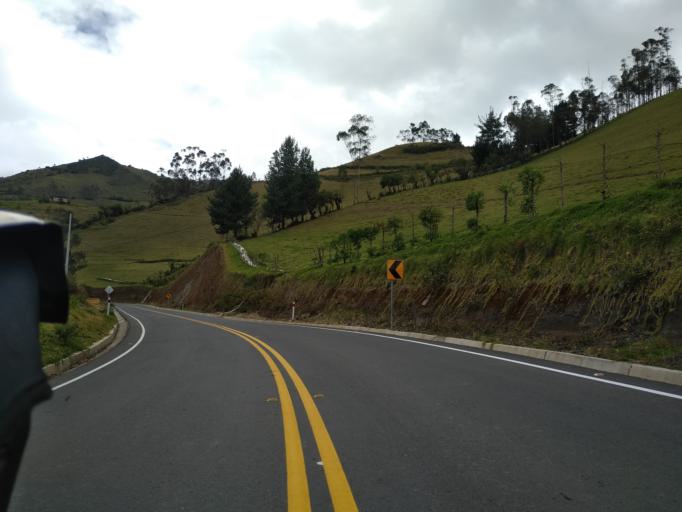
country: EC
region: Cotopaxi
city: Saquisili
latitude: -0.7525
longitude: -78.9060
